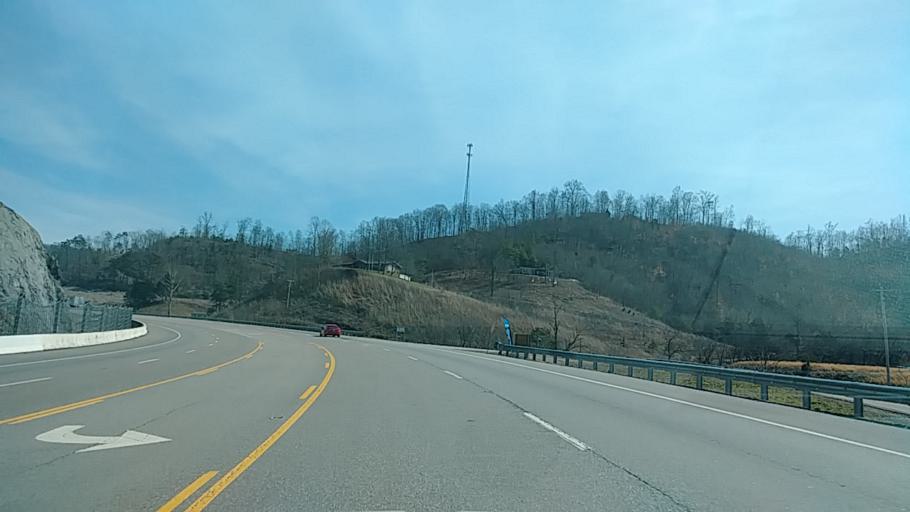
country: US
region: Tennessee
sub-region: Claiborne County
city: Tazewell
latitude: 36.4077
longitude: -83.4722
